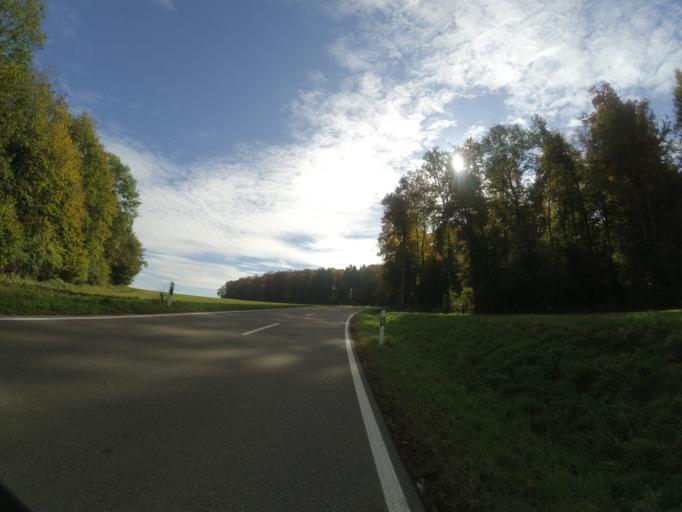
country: DE
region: Baden-Wuerttemberg
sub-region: Tuebingen Region
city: Amstetten
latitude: 48.6078
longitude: 9.9247
